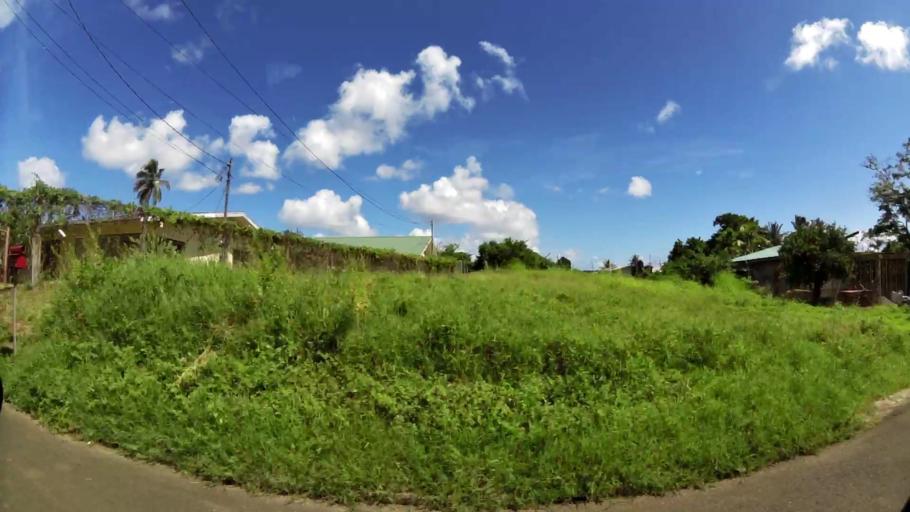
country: TT
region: Tobago
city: Scarborough
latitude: 11.1832
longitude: -60.8081
